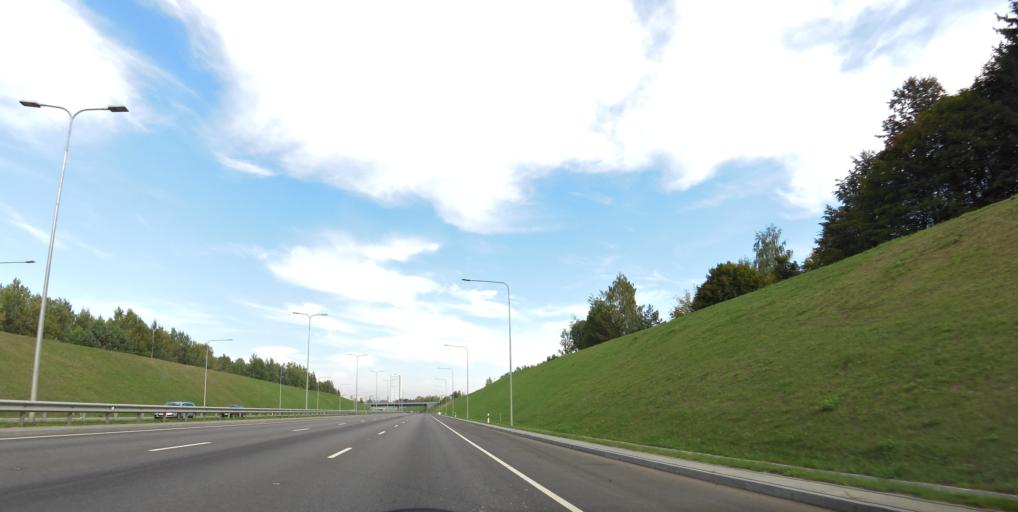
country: LT
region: Vilnius County
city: Pilaite
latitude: 54.6917
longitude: 25.2021
